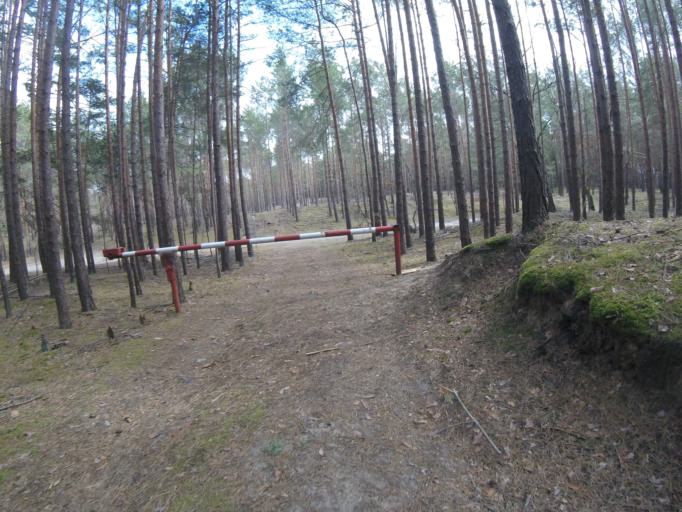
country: DE
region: Brandenburg
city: Gross Koris
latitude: 52.1874
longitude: 13.6588
